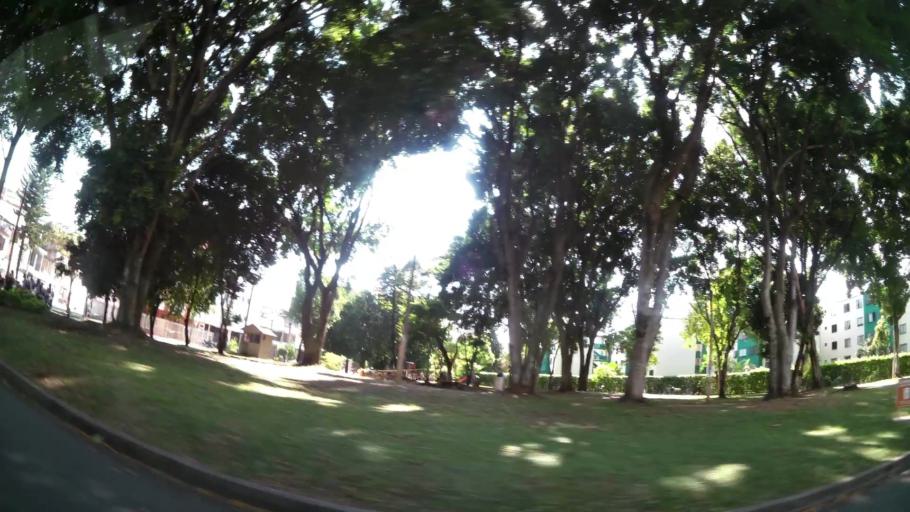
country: CO
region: Valle del Cauca
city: Cali
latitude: 3.4036
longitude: -76.5256
